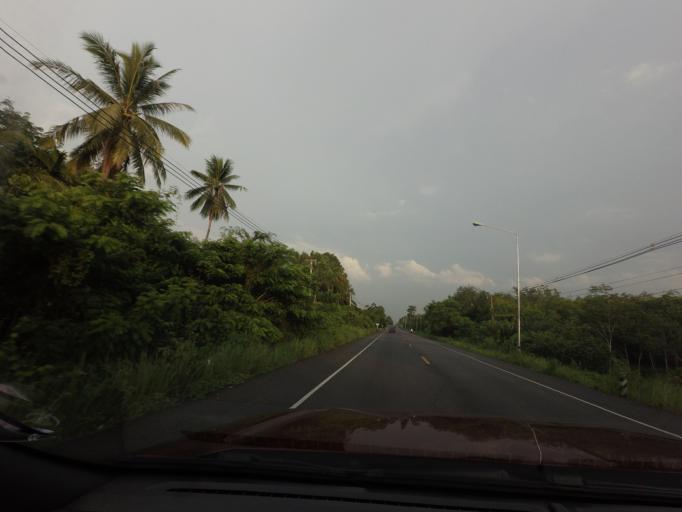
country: TH
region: Pattani
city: Mae Lan
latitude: 6.6602
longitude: 101.1686
